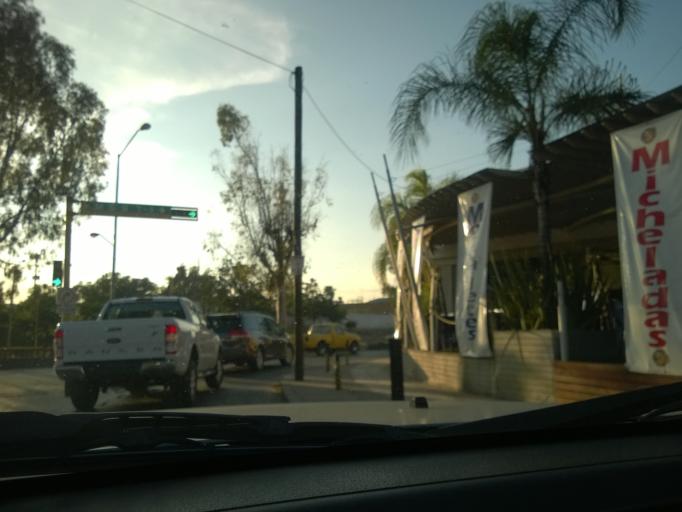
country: MX
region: Guanajuato
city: Leon
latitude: 21.1352
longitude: -101.6782
